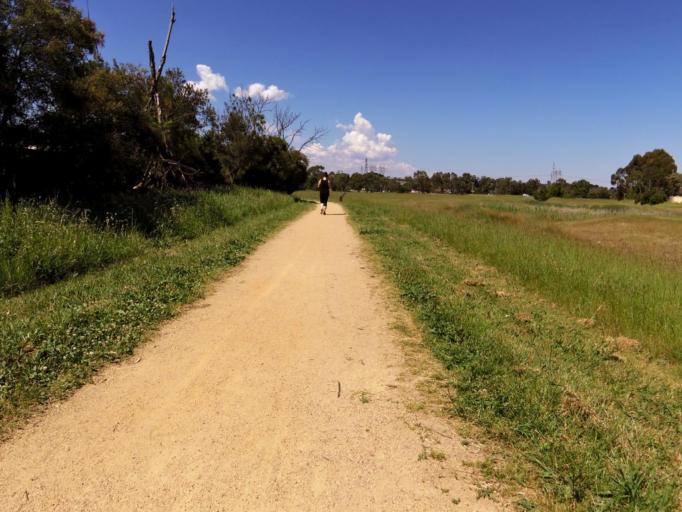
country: AU
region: Victoria
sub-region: Casey
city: Narre Warren South
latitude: -38.0366
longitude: 145.2758
